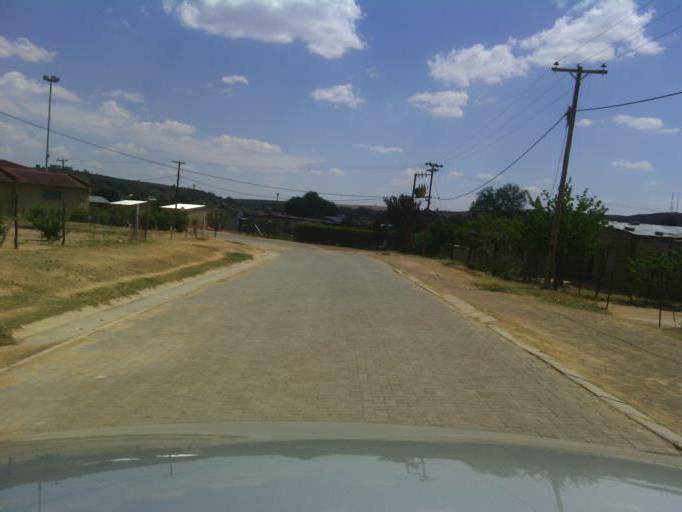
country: ZA
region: Orange Free State
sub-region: Xhariep District Municipality
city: Dewetsdorp
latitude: -29.5786
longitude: 26.6796
